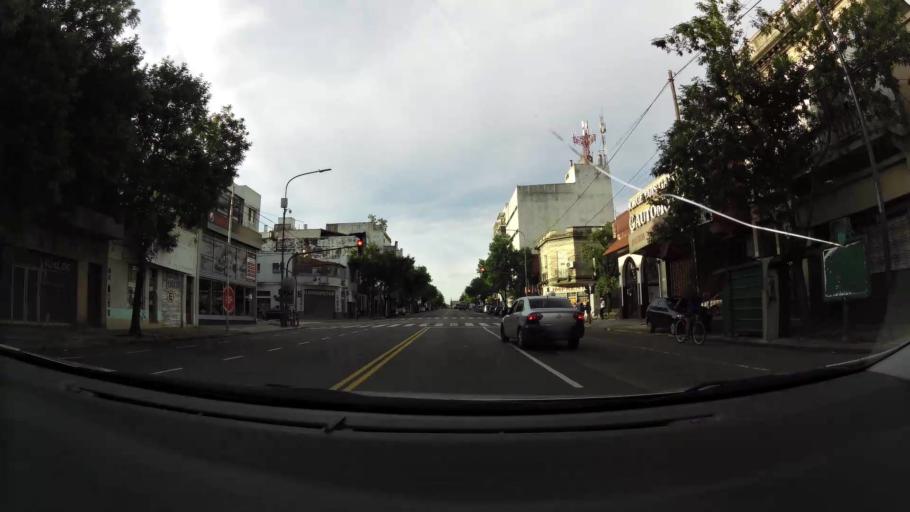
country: AR
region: Buenos Aires F.D.
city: Buenos Aires
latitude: -34.6384
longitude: -58.4240
